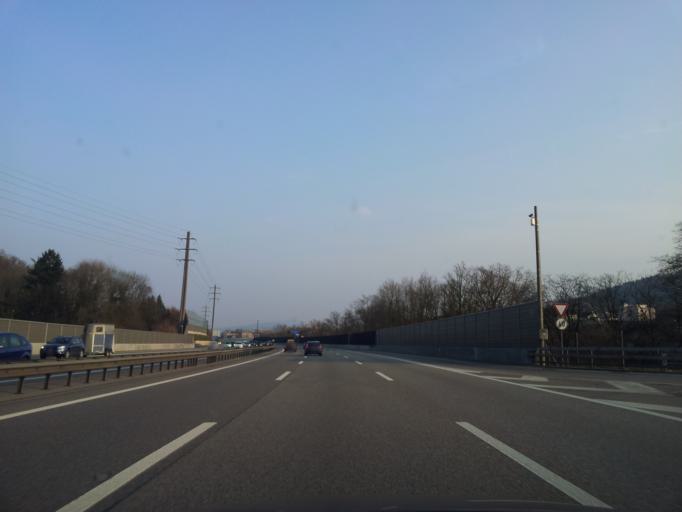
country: CH
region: Aargau
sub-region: Bezirk Baden
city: Killwangen
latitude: 47.4381
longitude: 8.3479
